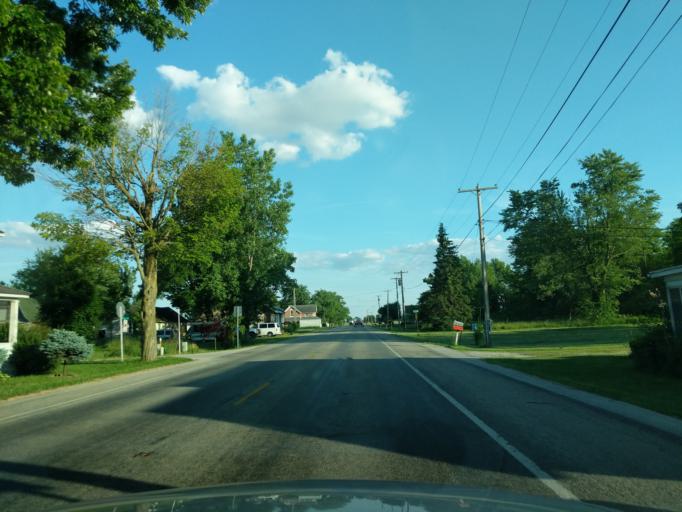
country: US
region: Indiana
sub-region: Huntington County
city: Warren
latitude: 40.7695
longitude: -85.4534
